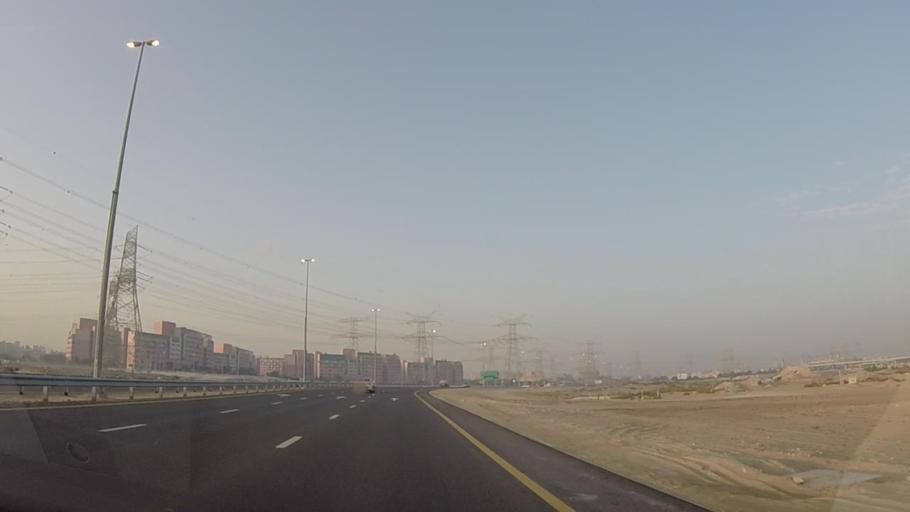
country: AE
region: Dubai
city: Dubai
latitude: 25.0543
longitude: 55.1349
